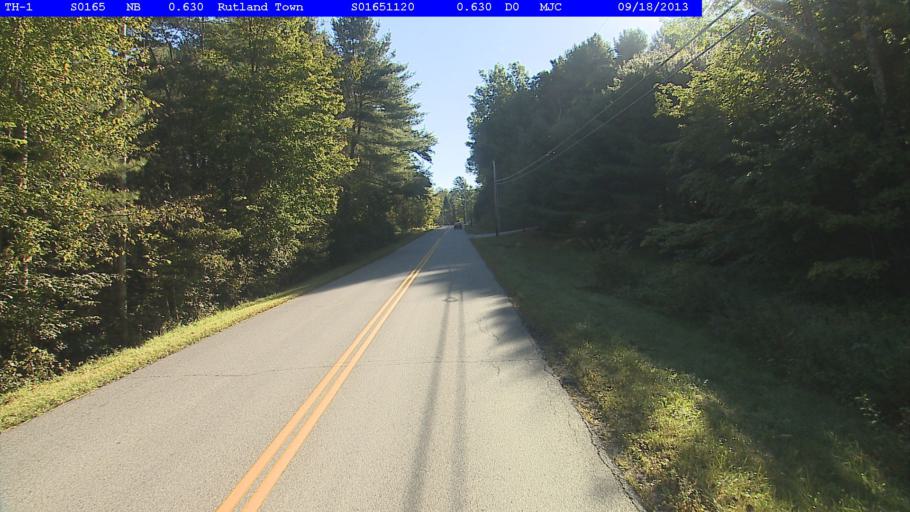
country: US
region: Vermont
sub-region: Rutland County
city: Rutland
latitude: 43.6520
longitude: -72.9597
